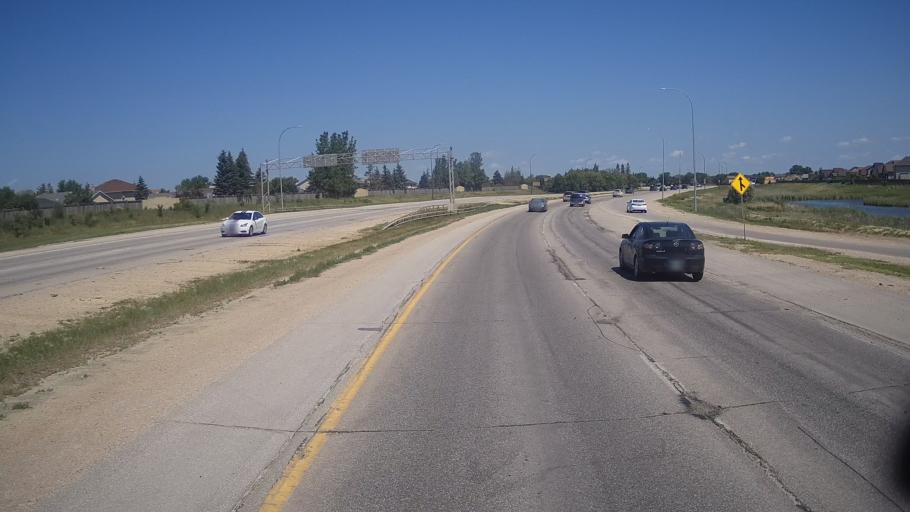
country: CA
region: Manitoba
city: Winnipeg
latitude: 49.9140
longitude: -97.0543
